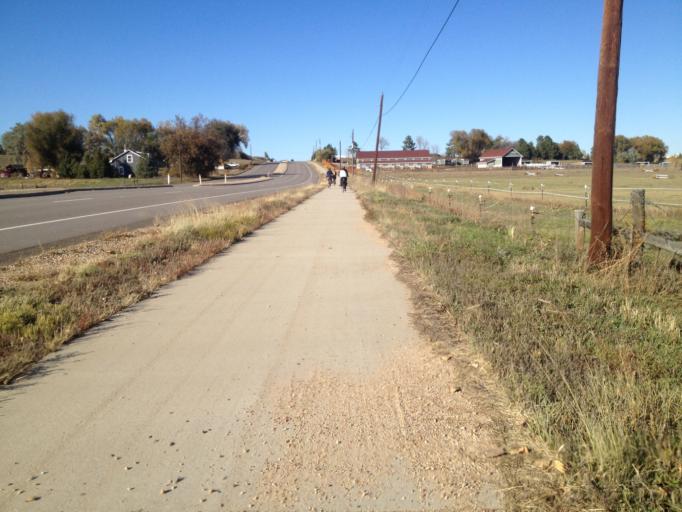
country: US
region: Colorado
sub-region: Boulder County
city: Niwot
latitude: 40.1279
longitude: -105.1497
